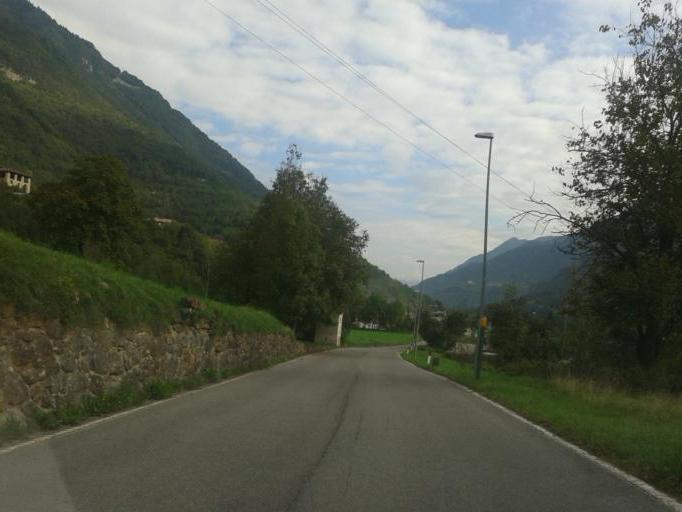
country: IT
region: Trentino-Alto Adige
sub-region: Provincia di Trento
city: Cimego
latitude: 45.9090
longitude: 10.6155
